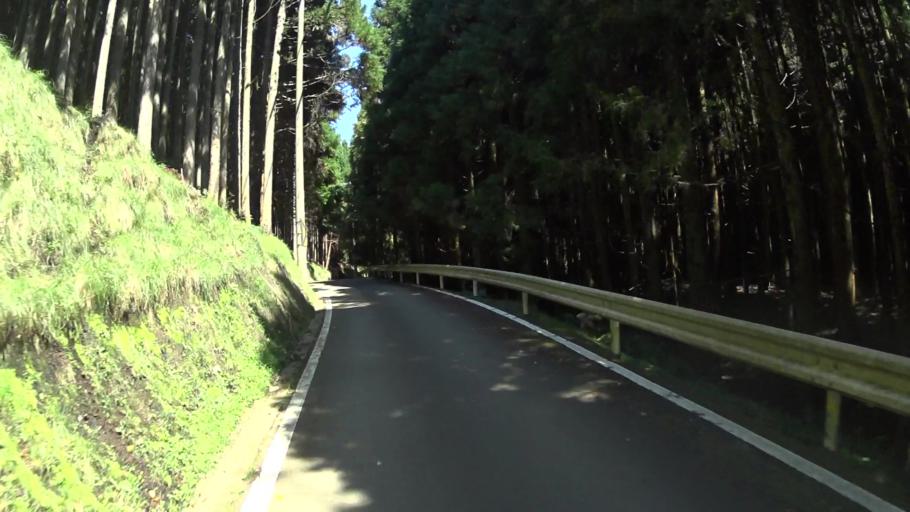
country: JP
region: Kyoto
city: Kameoka
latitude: 34.9599
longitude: 135.6240
